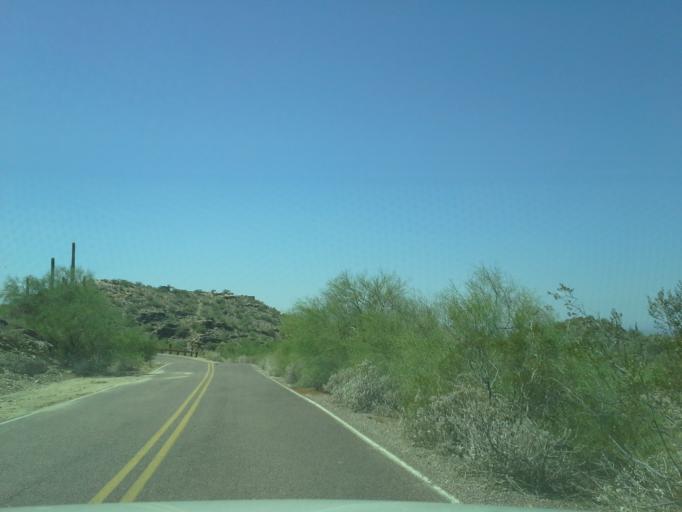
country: US
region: Arizona
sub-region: Maricopa County
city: Guadalupe
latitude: 33.3428
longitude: -112.0534
